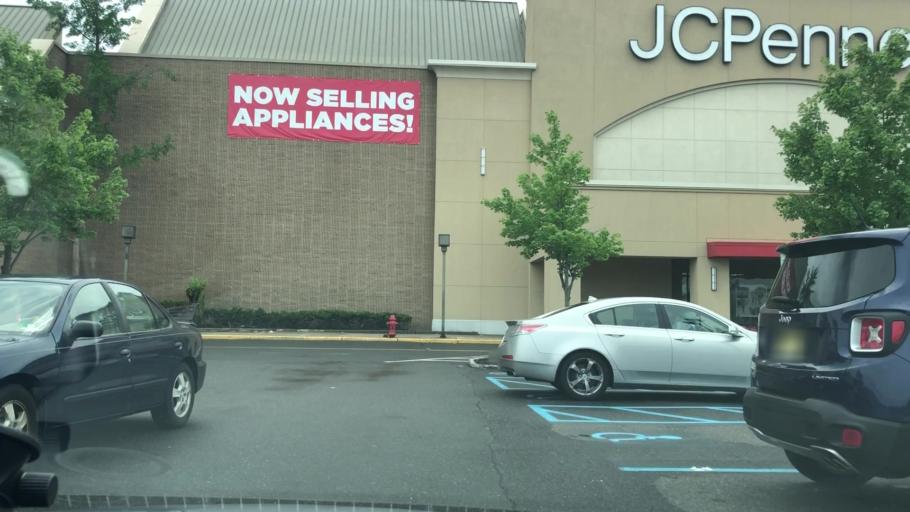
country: US
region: New Jersey
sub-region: Passaic County
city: Singac
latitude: 40.8911
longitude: -74.2529
